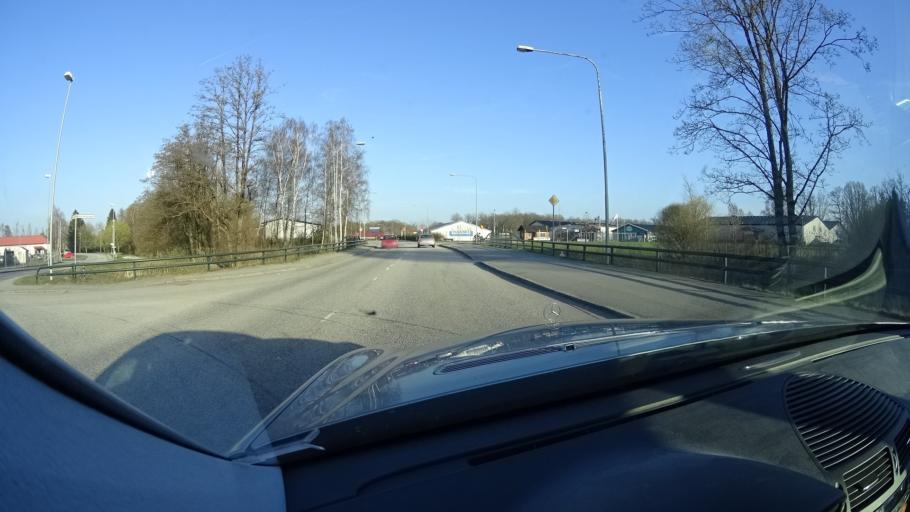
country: SE
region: Skane
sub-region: Hoors Kommun
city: Satofta
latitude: 55.9260
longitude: 13.5462
